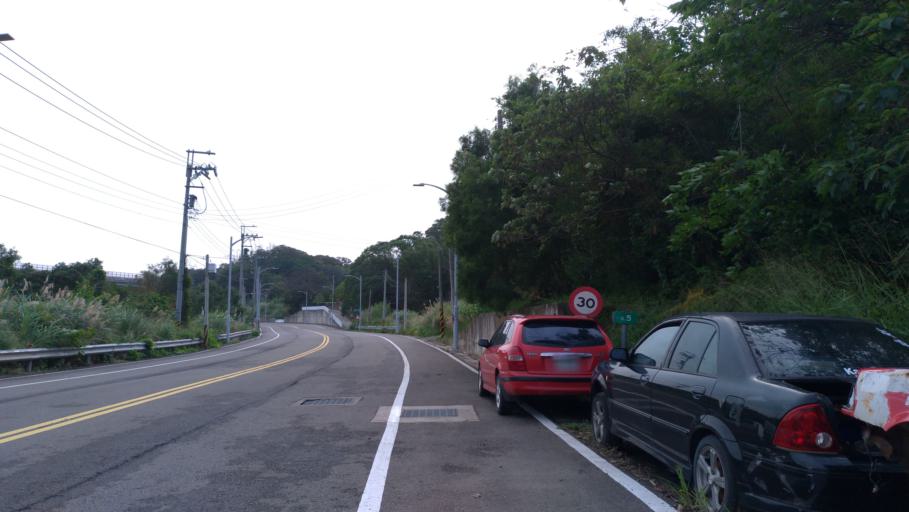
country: TW
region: Taiwan
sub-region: Hsinchu
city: Hsinchu
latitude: 24.7598
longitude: 120.9777
